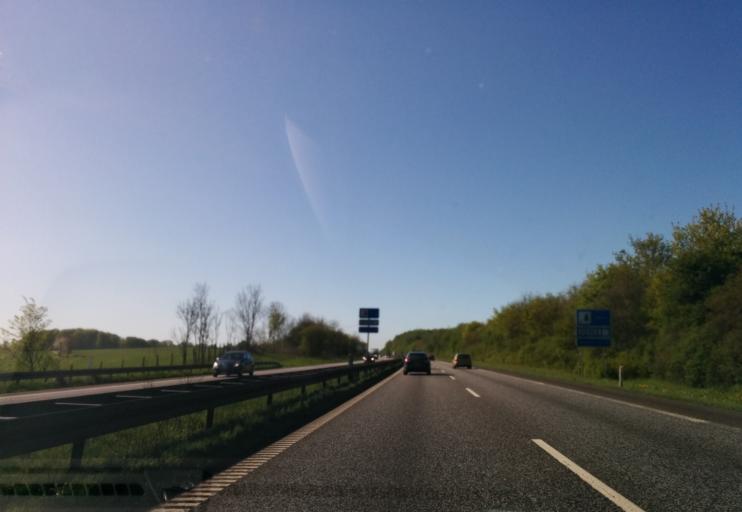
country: DK
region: Central Jutland
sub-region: Skanderborg Kommune
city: Skanderborg
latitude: 55.9922
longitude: 9.8676
